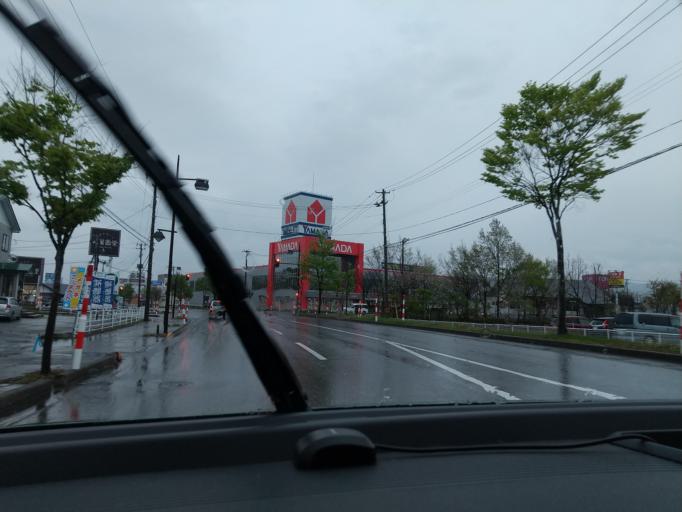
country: JP
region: Akita
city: Yokotemachi
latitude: 39.2962
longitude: 140.5505
